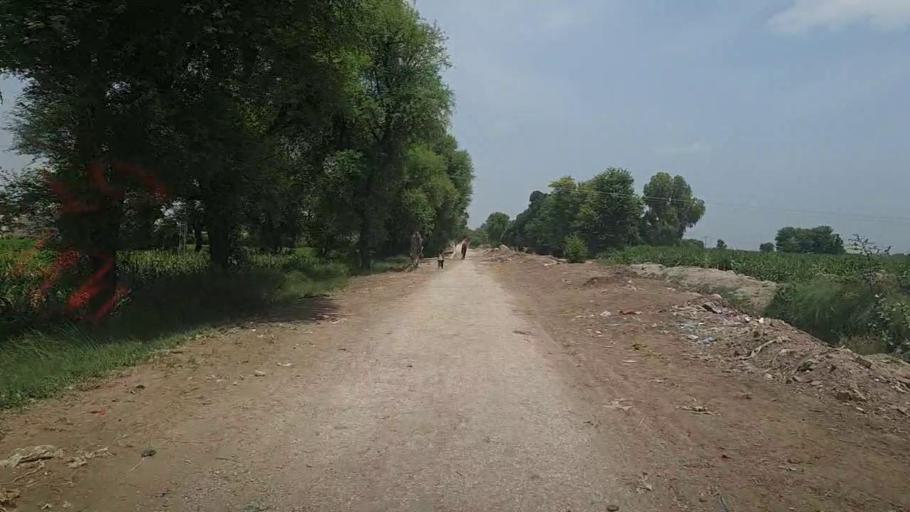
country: PK
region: Sindh
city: Ubauro
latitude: 28.2934
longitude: 69.8006
